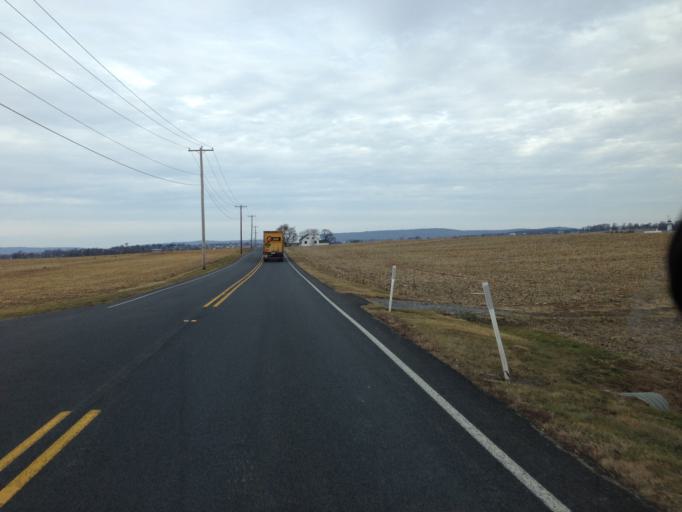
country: US
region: Pennsylvania
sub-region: Lancaster County
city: Manheim
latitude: 40.1583
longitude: -76.3647
